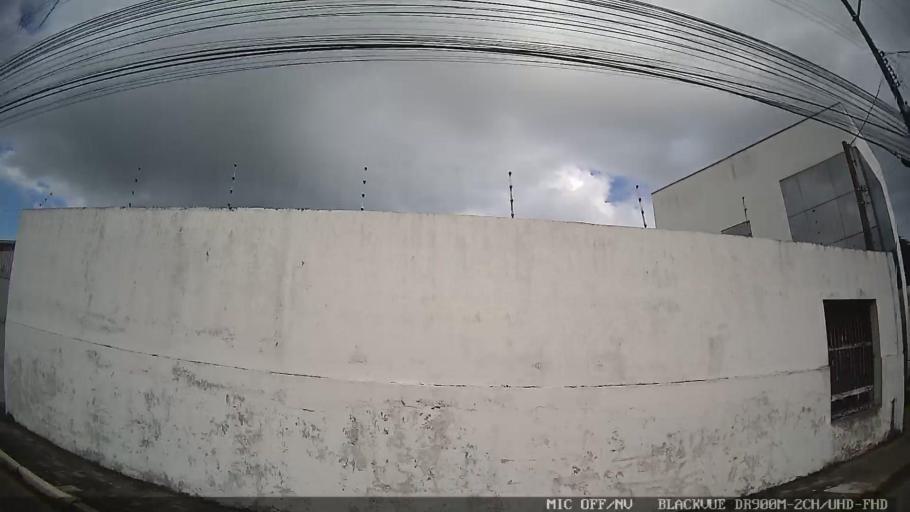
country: BR
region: Sao Paulo
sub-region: Itanhaem
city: Itanhaem
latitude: -24.1767
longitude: -46.7747
